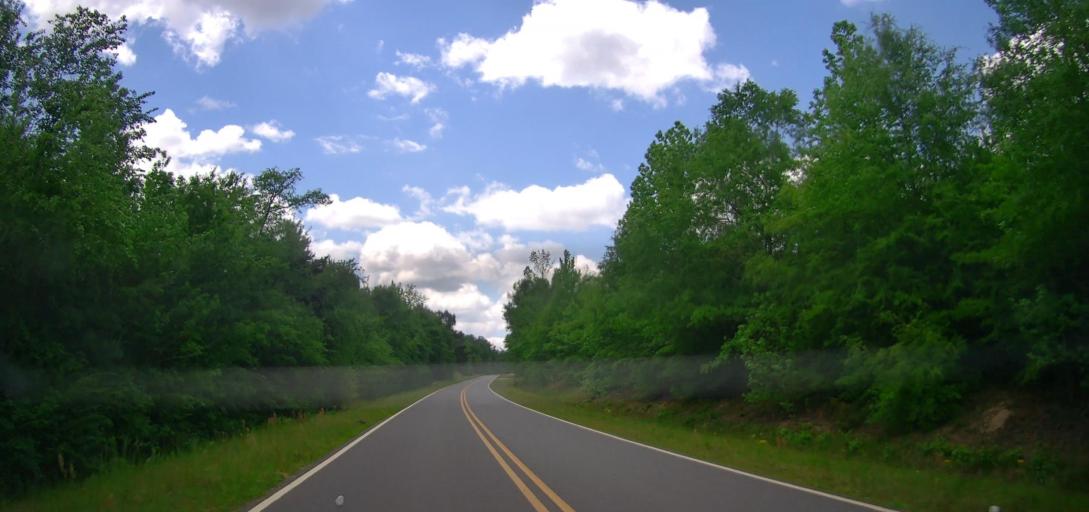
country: US
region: Georgia
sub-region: Laurens County
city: East Dublin
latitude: 32.6205
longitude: -82.8245
